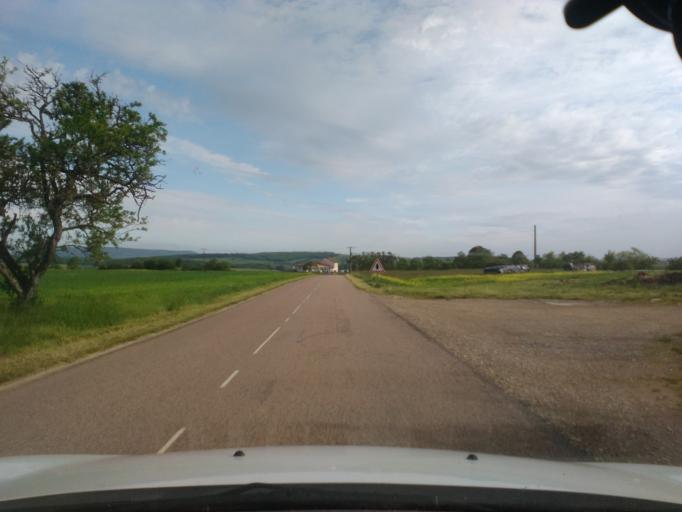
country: FR
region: Lorraine
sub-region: Departement des Vosges
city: Mirecourt
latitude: 48.3154
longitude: 6.1470
